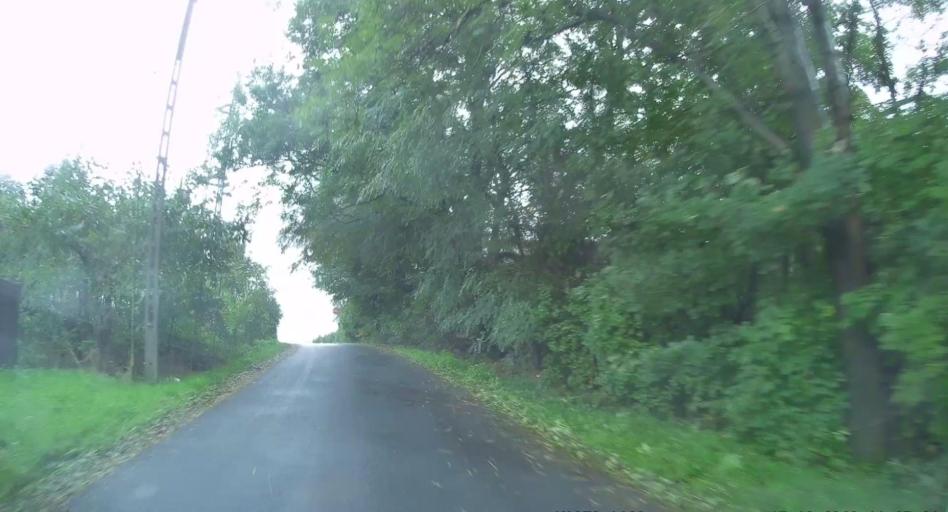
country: PL
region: Lesser Poland Voivodeship
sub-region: Powiat krakowski
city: Ochojno
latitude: 49.9834
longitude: 19.9891
